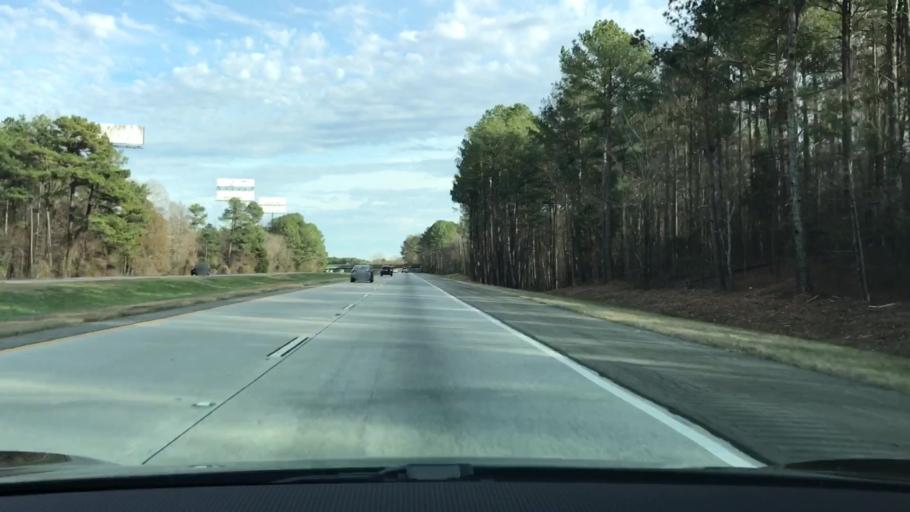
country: US
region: Georgia
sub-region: Taliaferro County
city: Crawfordville
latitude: 33.5284
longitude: -82.9629
